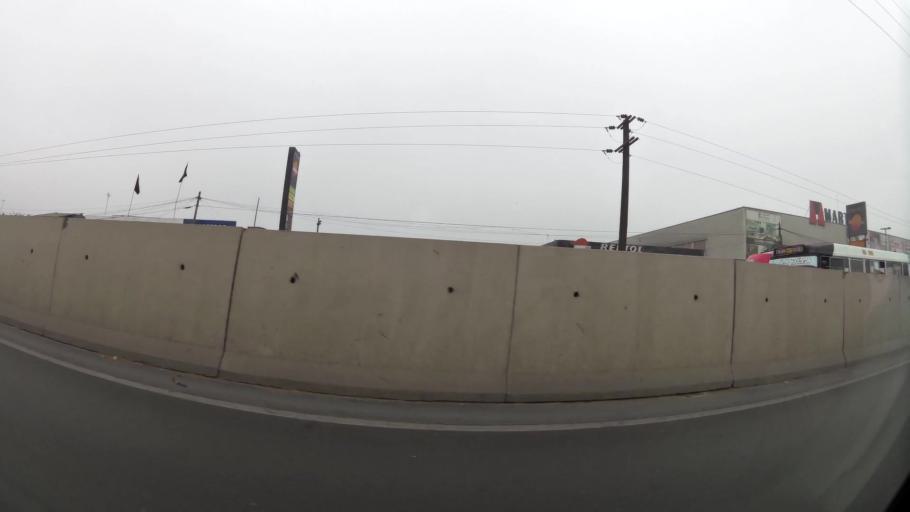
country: PE
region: Lima
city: Ventanilla
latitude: -11.8475
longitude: -77.0961
